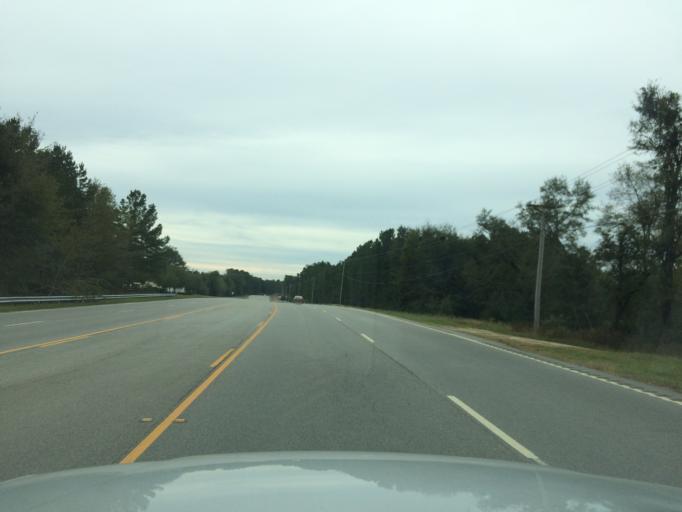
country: US
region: South Carolina
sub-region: Aiken County
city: Aiken
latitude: 33.6271
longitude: -81.6790
